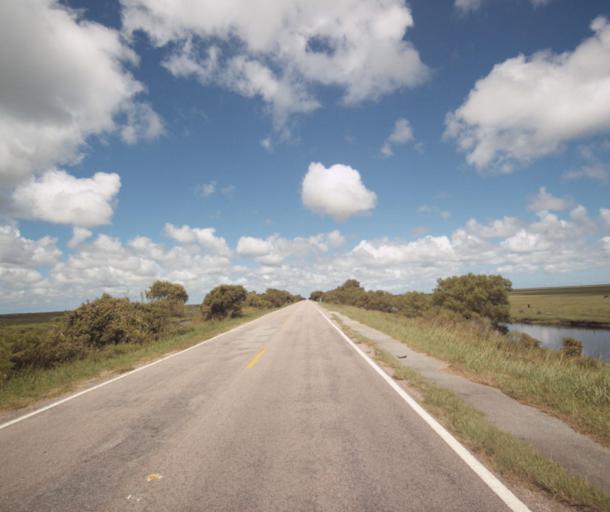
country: BR
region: Rio Grande do Sul
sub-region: Arroio Grande
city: Arroio Grande
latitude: -32.5464
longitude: -52.5435
